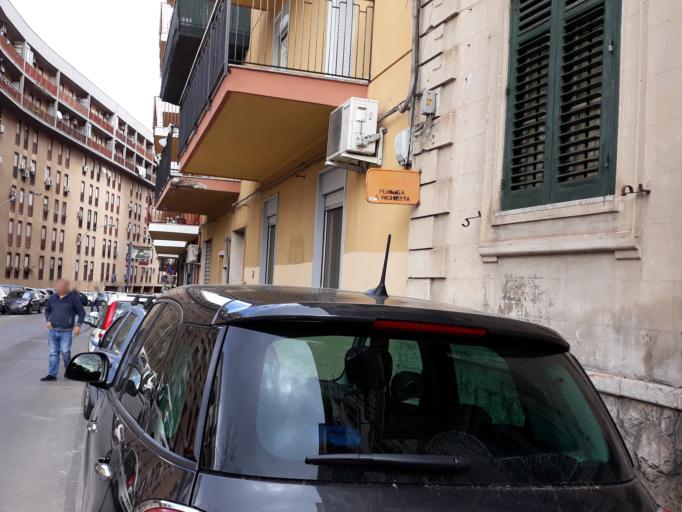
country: IT
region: Sicily
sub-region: Palermo
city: Palermo
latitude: 38.1067
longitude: 13.3449
